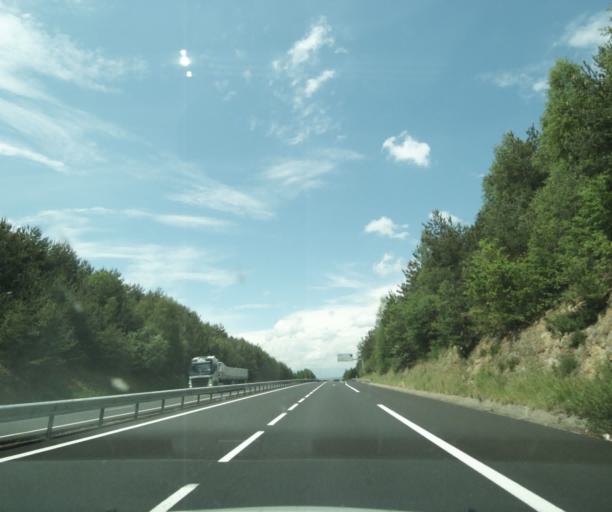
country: FR
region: Auvergne
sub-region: Departement du Cantal
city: Saint-Flour
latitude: 44.9982
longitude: 3.1741
